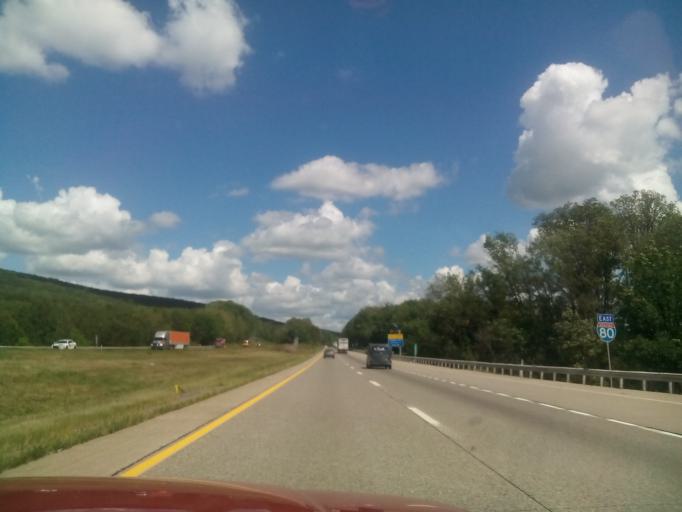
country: US
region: Pennsylvania
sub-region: Luzerne County
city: Conyngham
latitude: 41.0280
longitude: -76.0743
